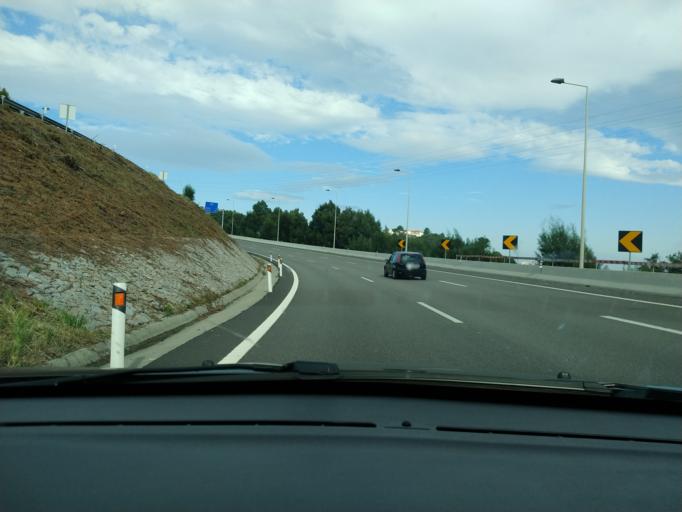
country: PT
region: Porto
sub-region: Vila Nova de Gaia
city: Perozinho
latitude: 41.0771
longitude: -8.5786
